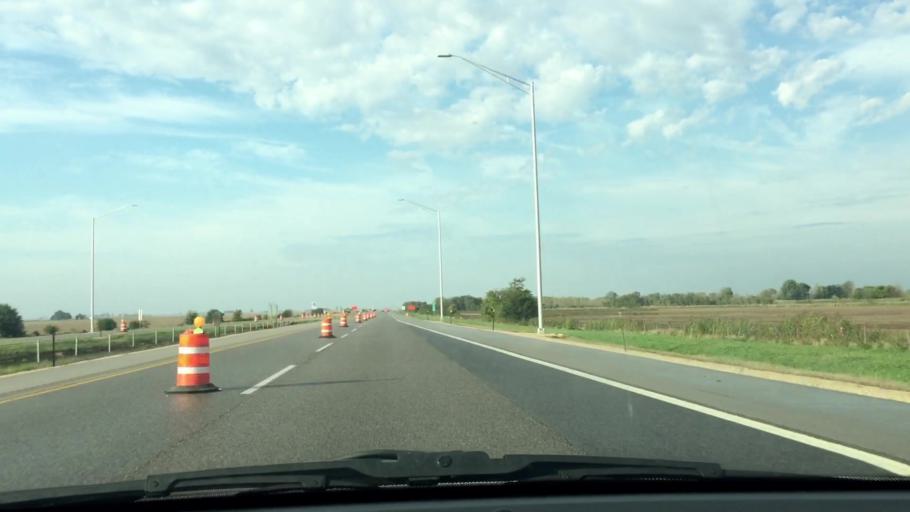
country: US
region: Illinois
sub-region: Ogle County
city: Rochelle
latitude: 41.8977
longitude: -89.0784
